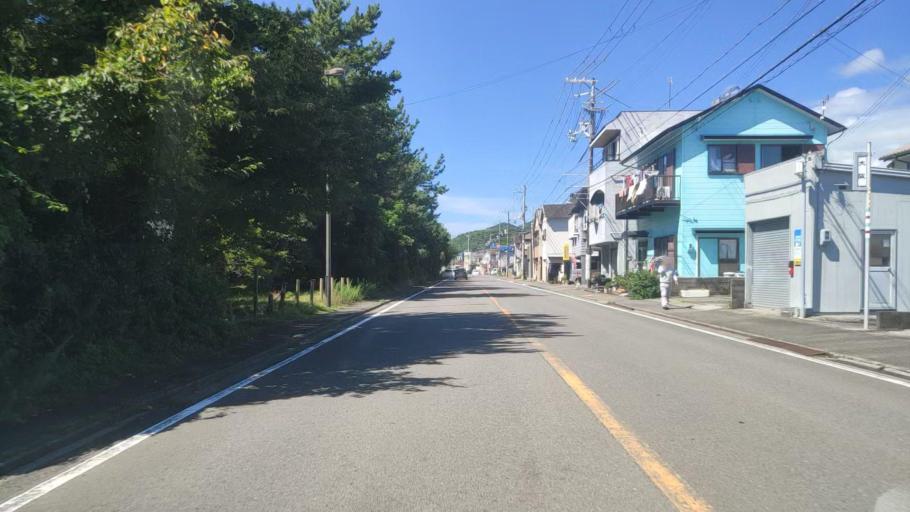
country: JP
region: Wakayama
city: Shingu
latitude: 33.7173
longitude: 136.0036
